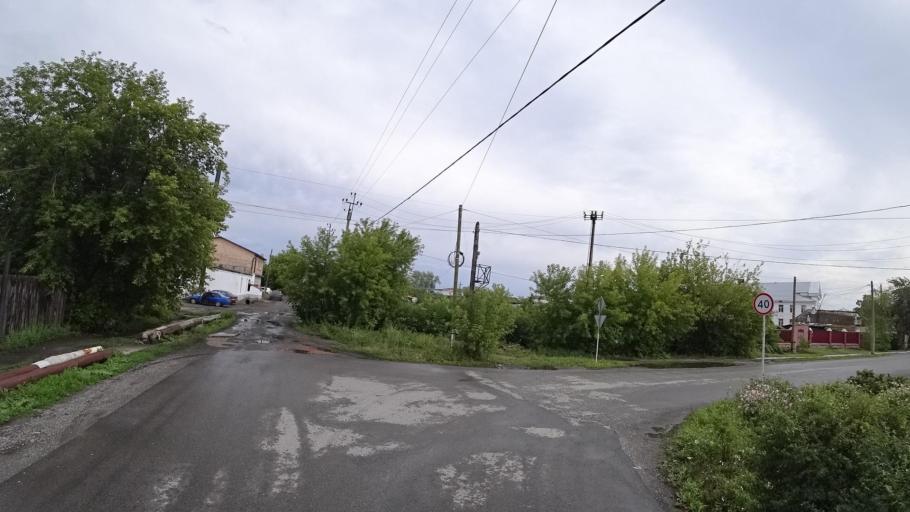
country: RU
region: Sverdlovsk
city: Kamyshlov
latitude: 56.8470
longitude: 62.7202
